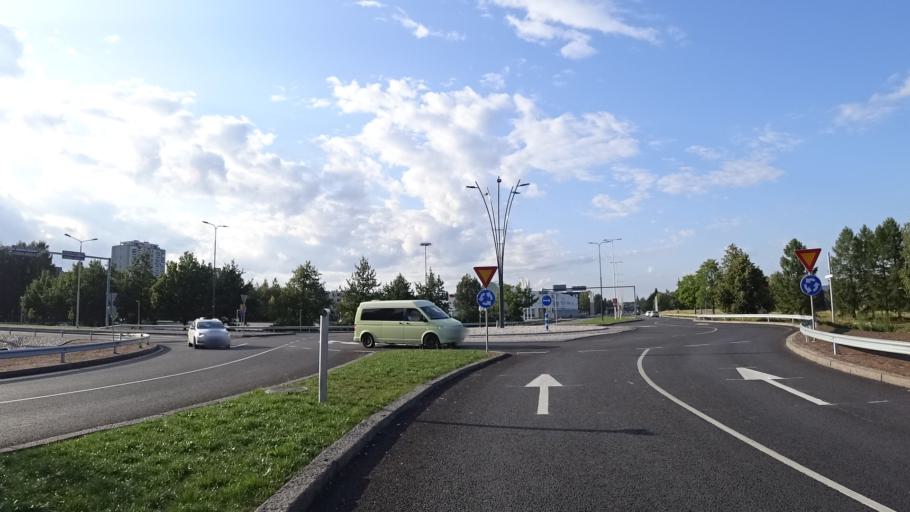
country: FI
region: South Karelia
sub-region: Imatra
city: Imatra
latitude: 61.1883
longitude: 28.7775
